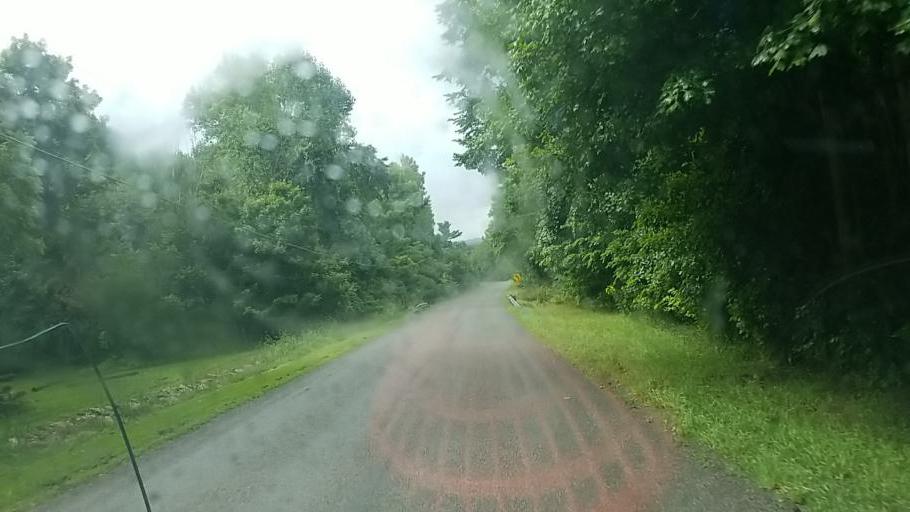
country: US
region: Ohio
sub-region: Champaign County
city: North Lewisburg
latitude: 40.3157
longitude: -83.6301
